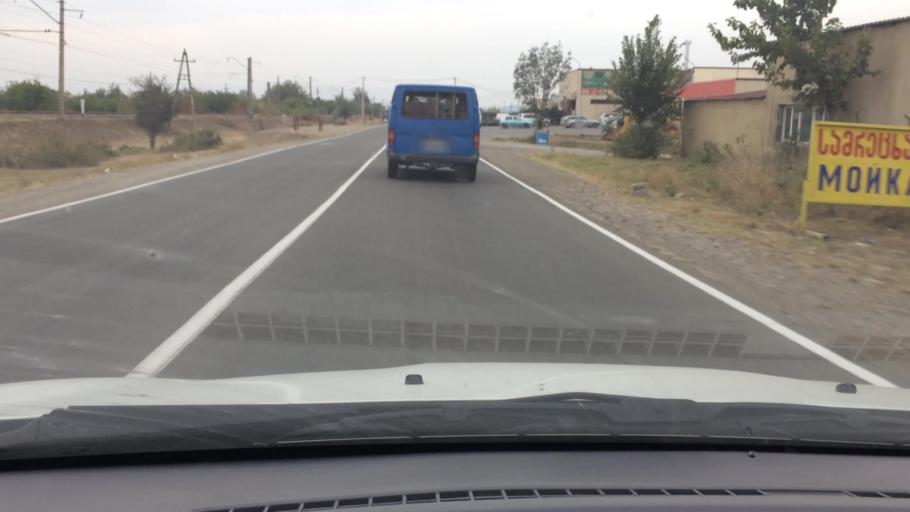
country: GE
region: Kvemo Kartli
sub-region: Marneuli
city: Marneuli
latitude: 41.4378
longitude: 44.8185
